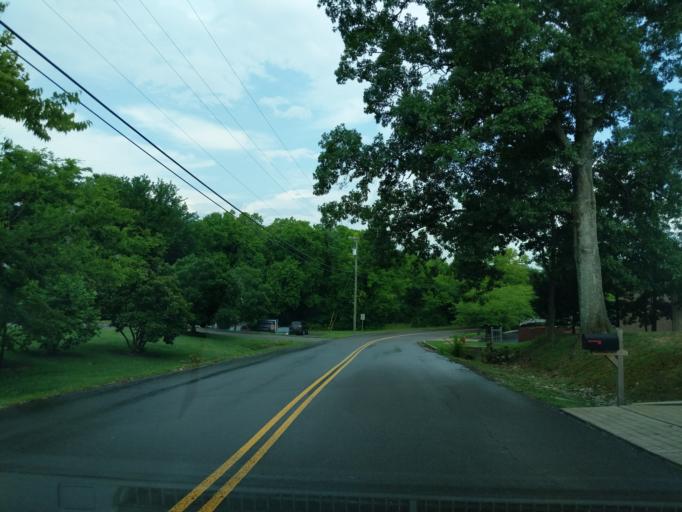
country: US
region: Tennessee
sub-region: Cheatham County
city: Pegram
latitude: 36.0444
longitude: -86.9602
